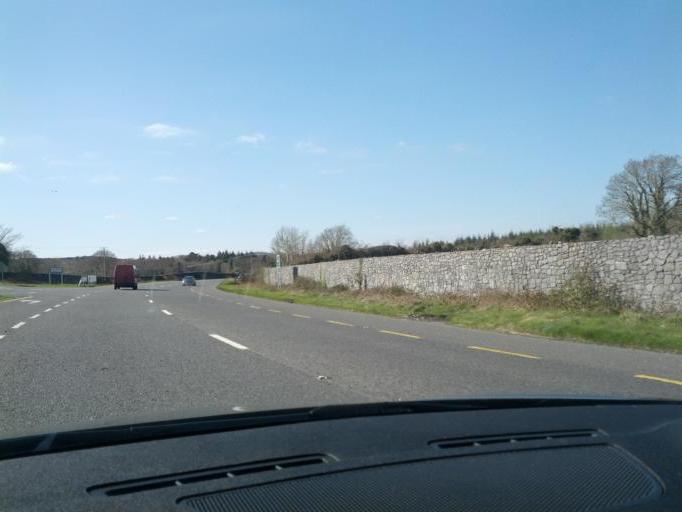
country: IE
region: Connaught
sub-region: County Galway
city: Moycullen
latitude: 53.3096
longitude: -9.1401
